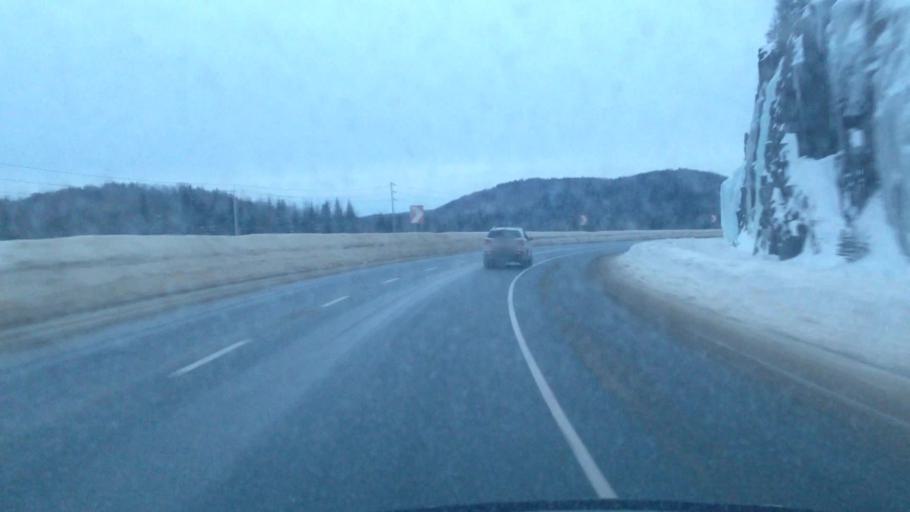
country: CA
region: Quebec
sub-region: Laurentides
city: Sainte-Agathe-des-Monts
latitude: 46.1101
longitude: -74.4200
